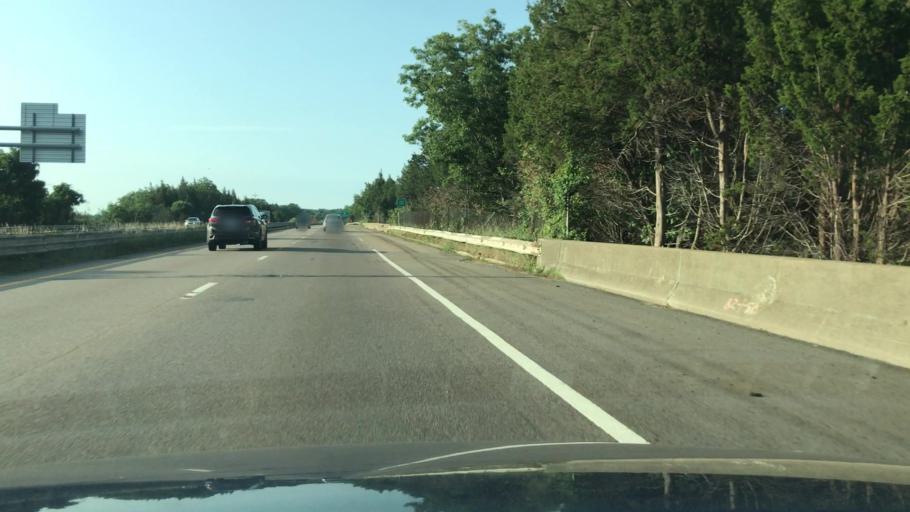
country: US
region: Massachusetts
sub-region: Plymouth County
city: Kingston
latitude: 41.9982
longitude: -70.7217
